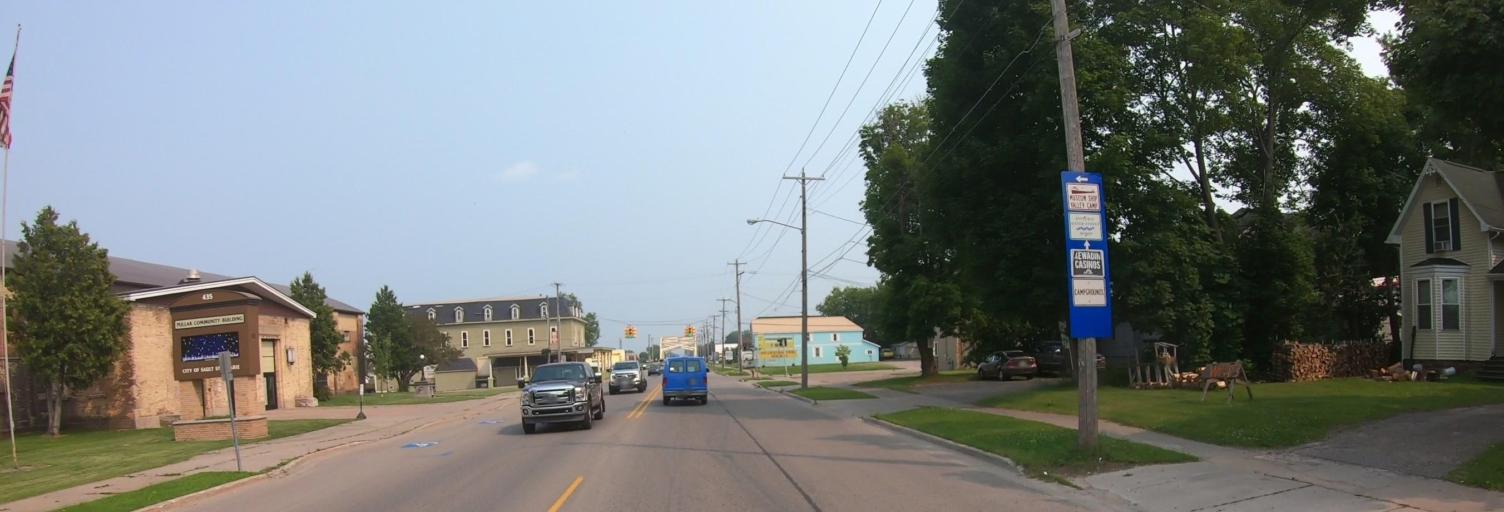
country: US
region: Michigan
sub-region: Chippewa County
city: Sault Ste. Marie
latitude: 46.4978
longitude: -84.3386
